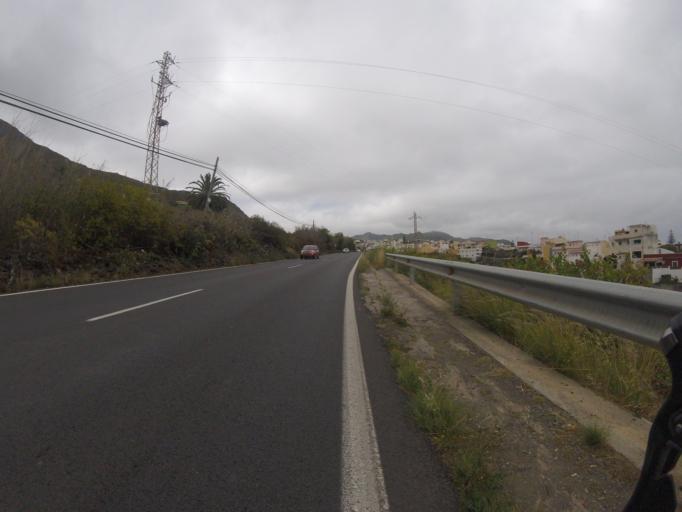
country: ES
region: Canary Islands
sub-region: Provincia de Santa Cruz de Tenerife
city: Tegueste
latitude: 28.5403
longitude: -16.3580
